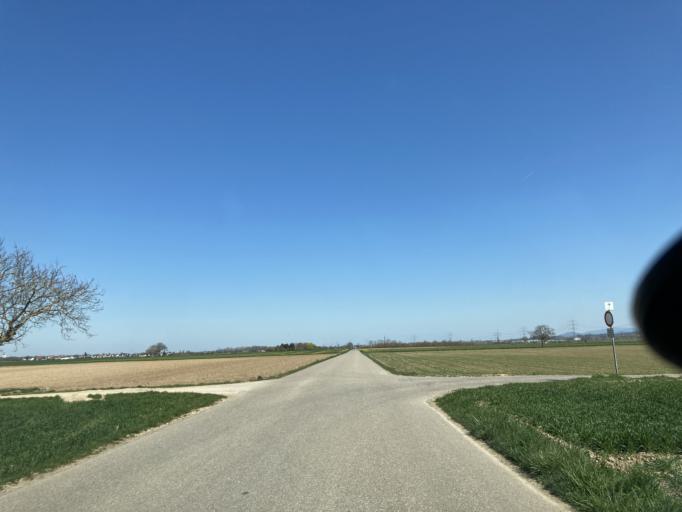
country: DE
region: Baden-Wuerttemberg
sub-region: Freiburg Region
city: Neuenburg am Rhein
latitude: 47.7887
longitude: 7.5681
